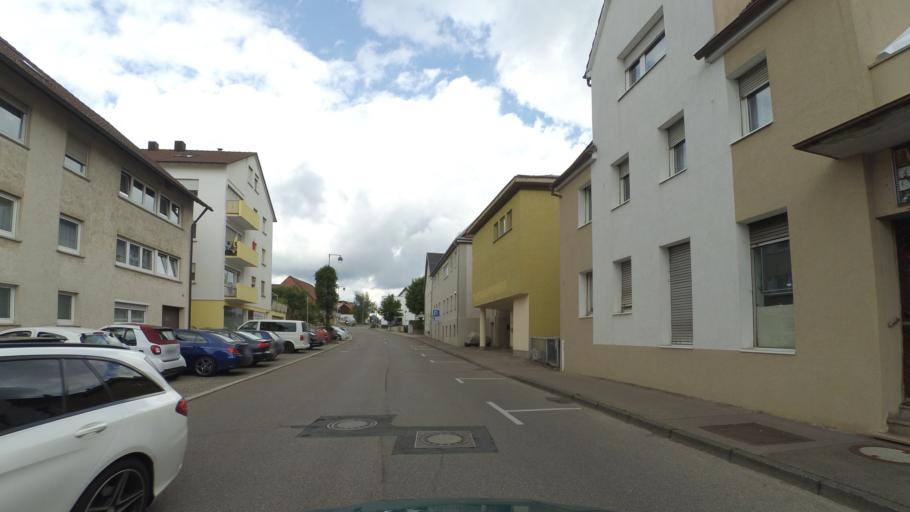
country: DE
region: Baden-Wuerttemberg
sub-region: Regierungsbezirk Stuttgart
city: Salach
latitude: 48.6923
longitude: 9.7402
